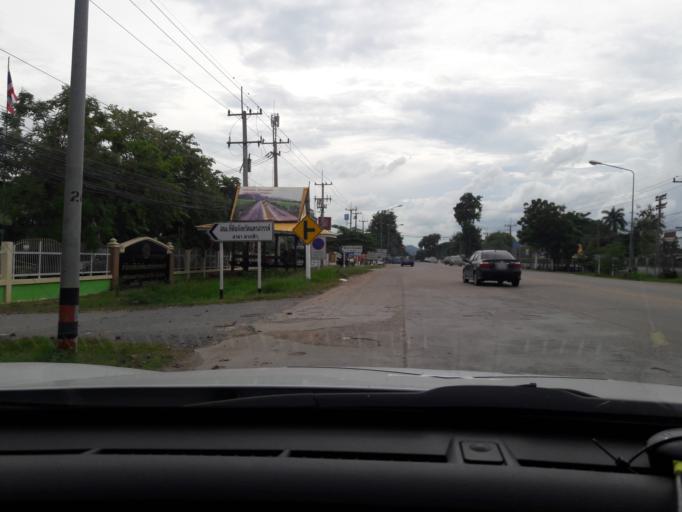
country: TH
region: Nakhon Sawan
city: Tak Fa
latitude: 15.3480
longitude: 100.4961
